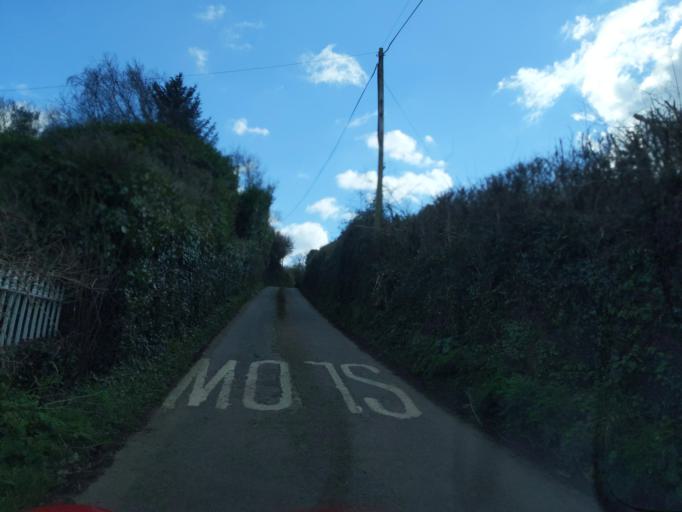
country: GB
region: England
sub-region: Devon
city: Salcombe
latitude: 50.2510
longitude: -3.7014
